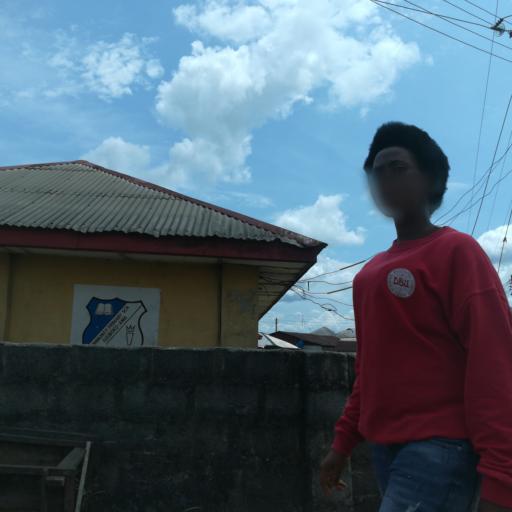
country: NG
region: Rivers
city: Port Harcourt
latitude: 4.7759
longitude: 7.0431
